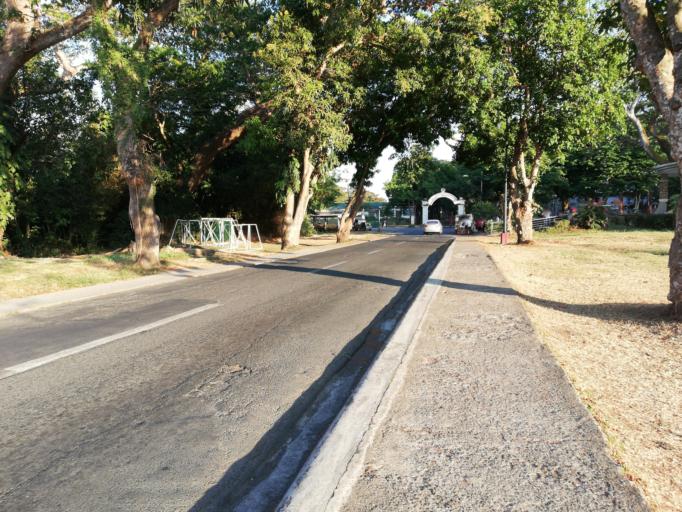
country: PH
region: Calabarzon
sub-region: Province of Laguna
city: Los Banos
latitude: 14.1604
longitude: 121.2432
